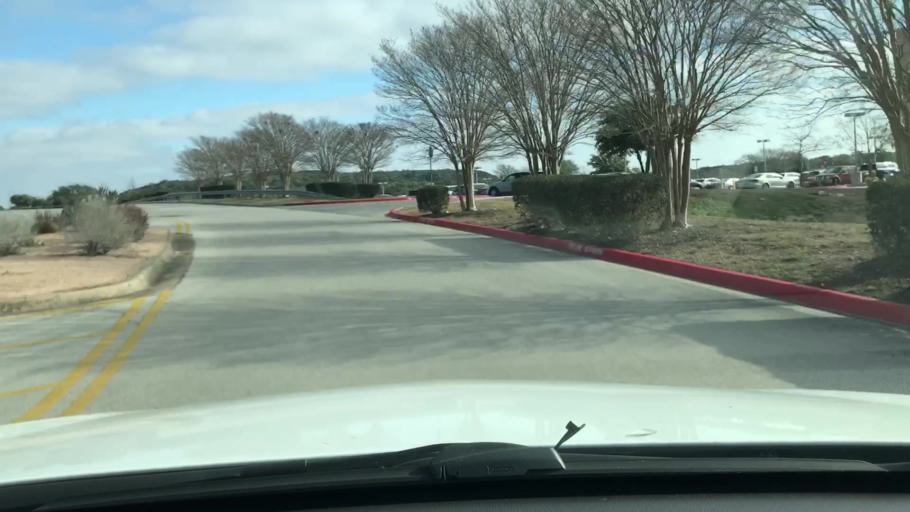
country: US
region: Texas
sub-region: Travis County
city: Bee Cave
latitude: 30.3171
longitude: -97.9550
